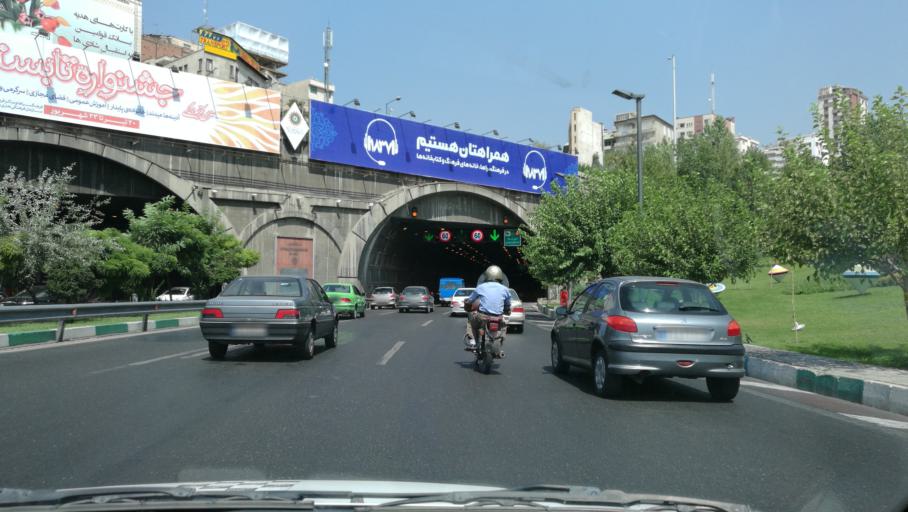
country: IR
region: Tehran
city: Tehran
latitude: 35.7405
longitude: 51.4163
